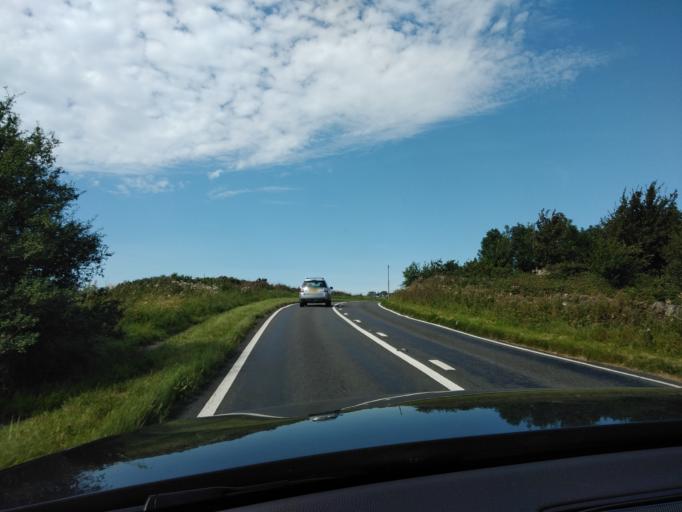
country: GB
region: England
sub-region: Derbyshire
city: Dronfield
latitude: 53.2955
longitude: -1.5453
